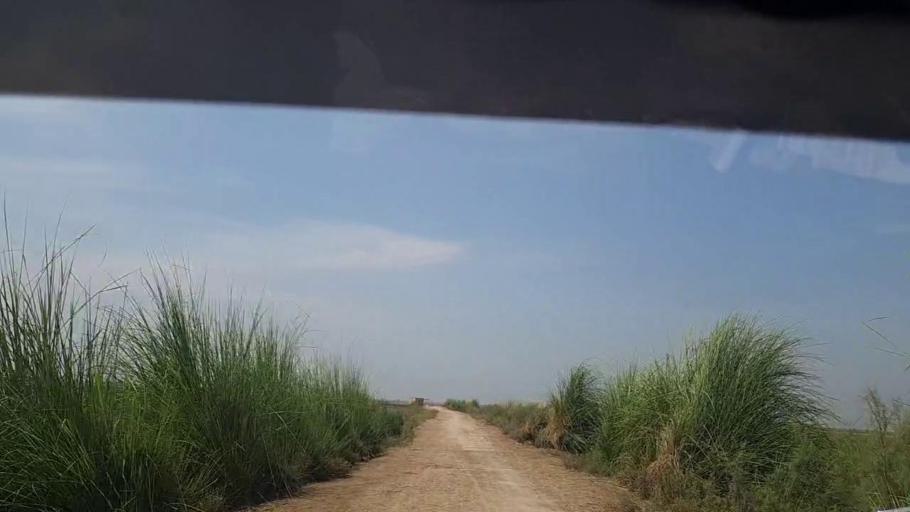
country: PK
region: Sindh
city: Thul
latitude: 28.2194
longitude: 68.6761
